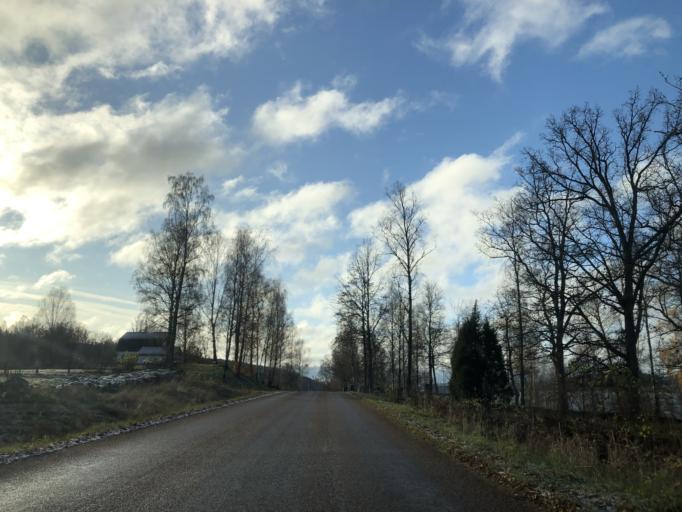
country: SE
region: Vaestra Goetaland
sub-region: Ulricehamns Kommun
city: Ulricehamn
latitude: 57.7681
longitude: 13.3991
